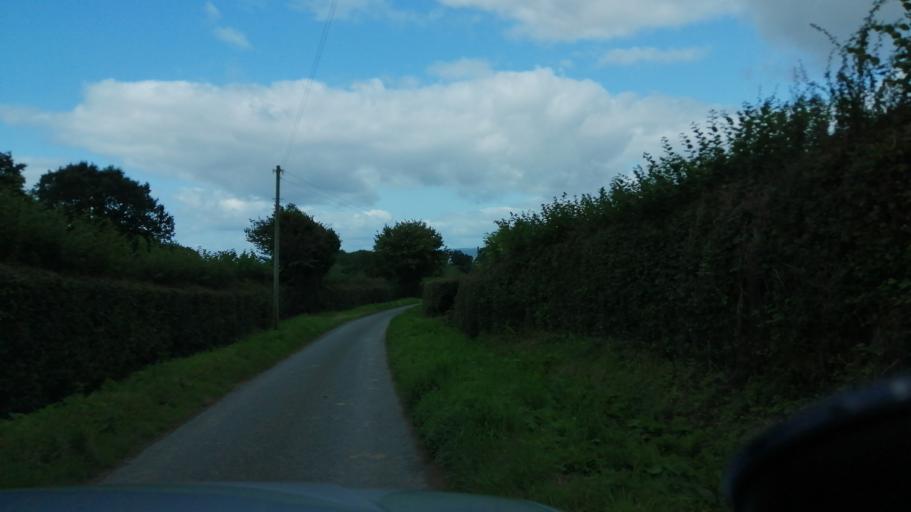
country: GB
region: England
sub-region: Herefordshire
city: Yazor
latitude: 52.1220
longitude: -2.9082
